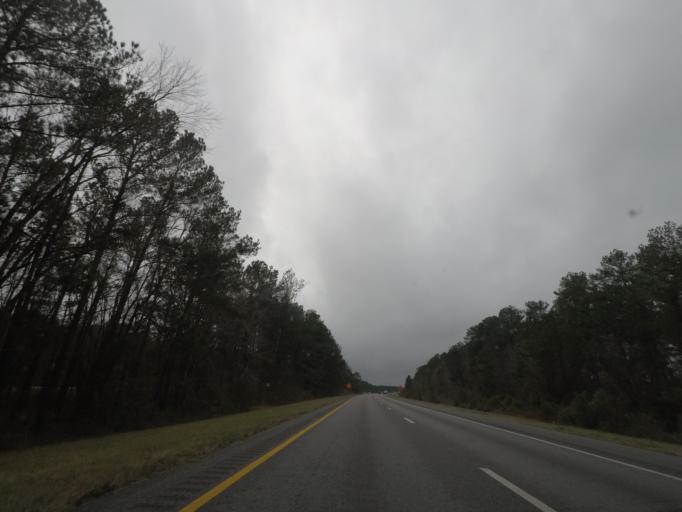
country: US
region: South Carolina
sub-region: Orangeburg County
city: Holly Hill
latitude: 33.3296
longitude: -80.5408
